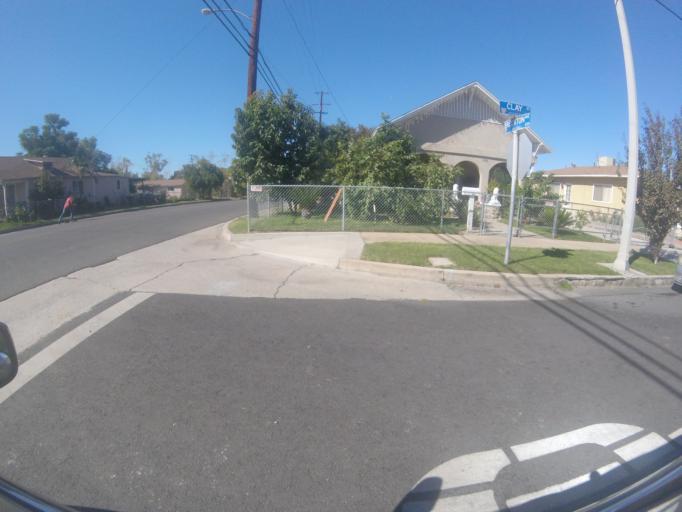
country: US
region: California
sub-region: San Bernardino County
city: Redlands
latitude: 34.0665
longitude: -117.1847
